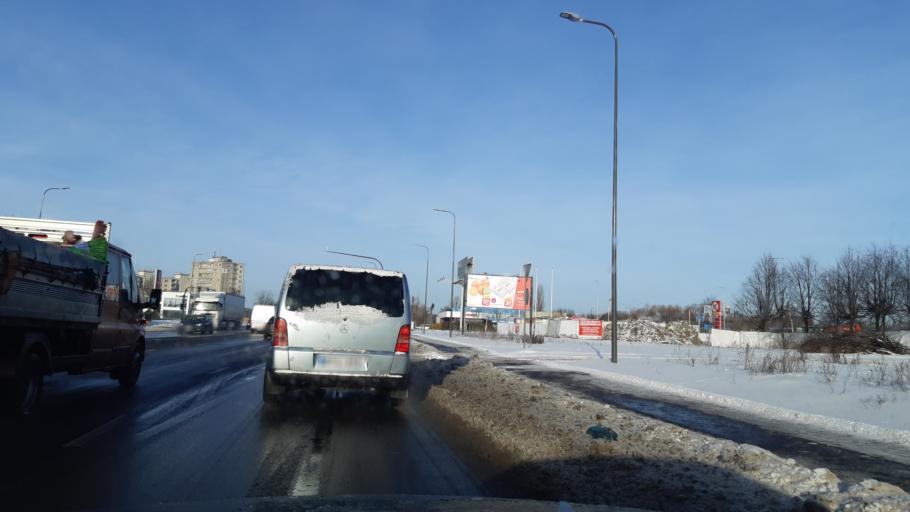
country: LT
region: Kauno apskritis
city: Dainava (Kaunas)
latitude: 54.9271
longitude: 23.9739
